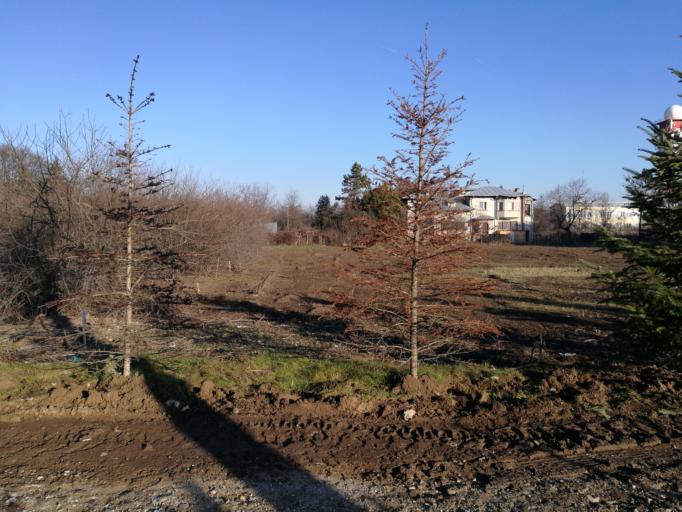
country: RO
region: Ilfov
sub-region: Comuna Otopeni
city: Otopeni
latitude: 44.5120
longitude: 26.0754
